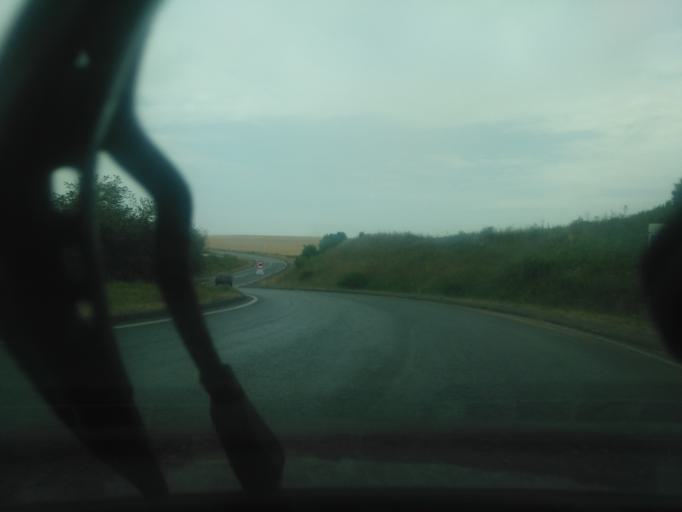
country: FR
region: Poitou-Charentes
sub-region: Departement de la Vienne
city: Cisse
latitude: 46.6296
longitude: 0.2637
